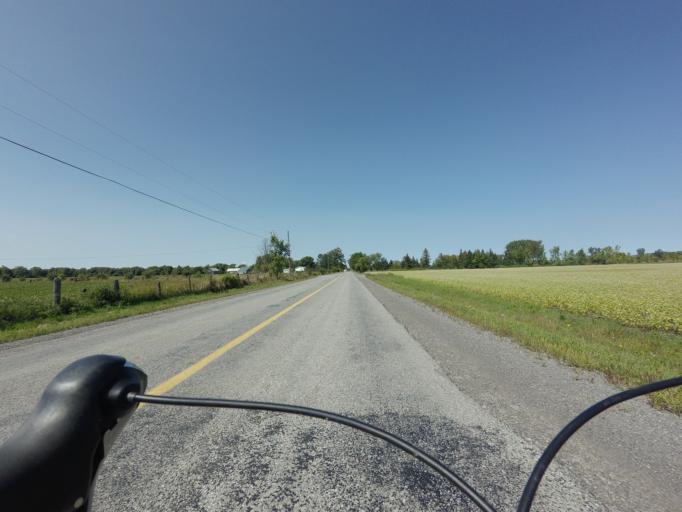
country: CA
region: Ontario
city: Bells Corners
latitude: 45.4365
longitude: -76.0656
